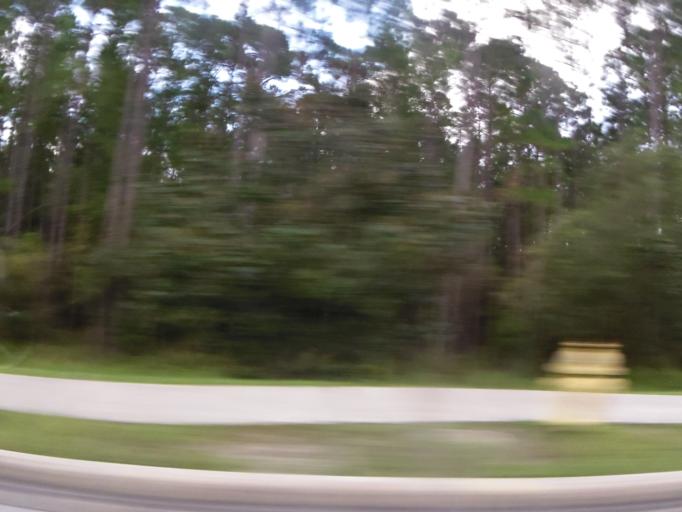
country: US
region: Florida
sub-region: Saint Johns County
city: Fruit Cove
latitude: 30.0798
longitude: -81.6025
